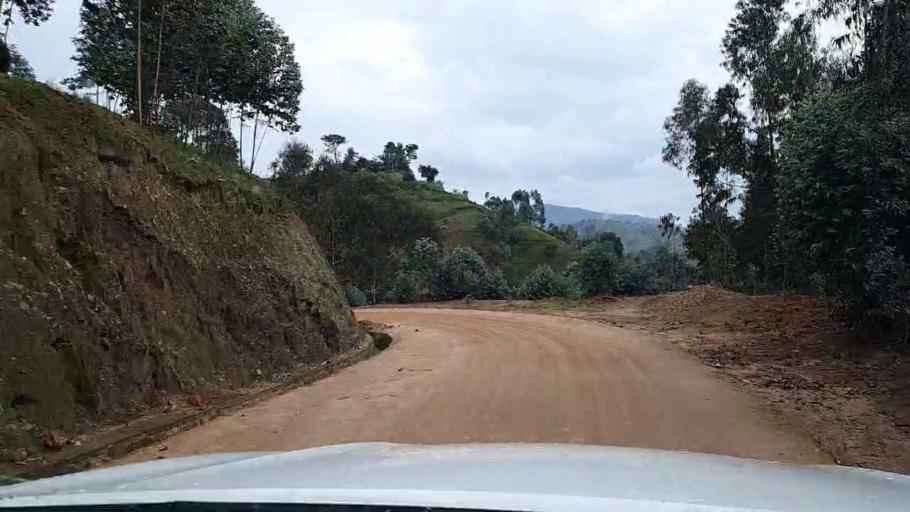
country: RW
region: Southern Province
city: Nzega
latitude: -2.4540
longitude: 29.4665
